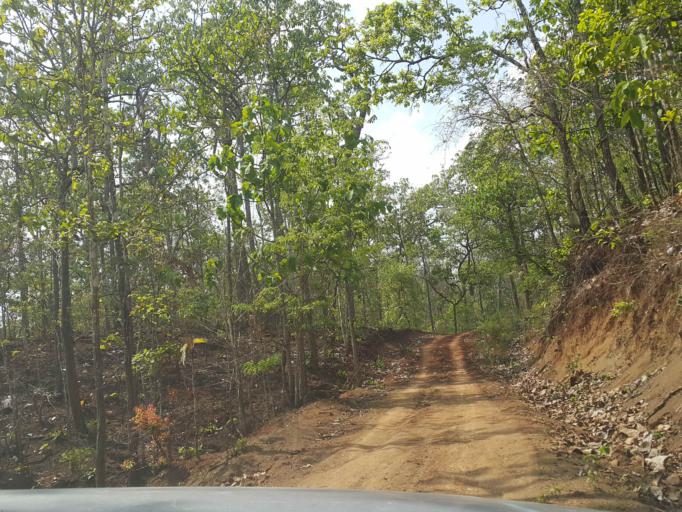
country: TH
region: Chiang Mai
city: Wiang Haeng
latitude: 19.3267
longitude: 98.7201
